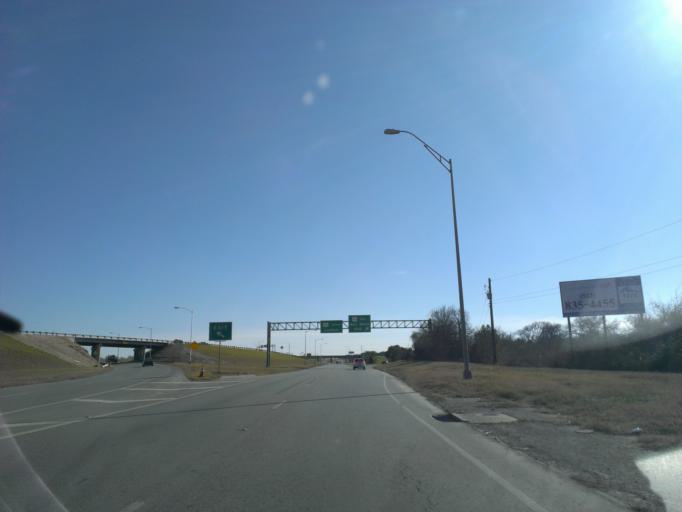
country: US
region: Texas
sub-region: Travis County
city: Austin
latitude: 30.2265
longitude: -97.6833
